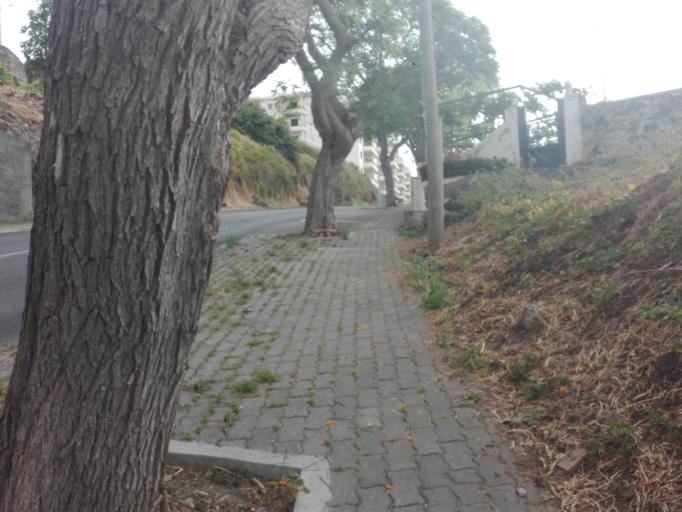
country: PT
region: Madeira
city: Canico
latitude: 32.6482
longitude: -16.8274
